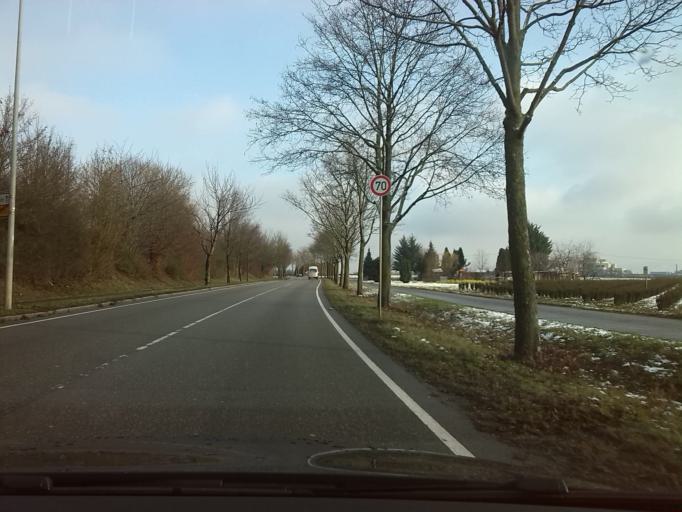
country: DE
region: Baden-Wuerttemberg
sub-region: Regierungsbezirk Stuttgart
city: Fellbach
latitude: 48.8194
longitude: 9.2841
